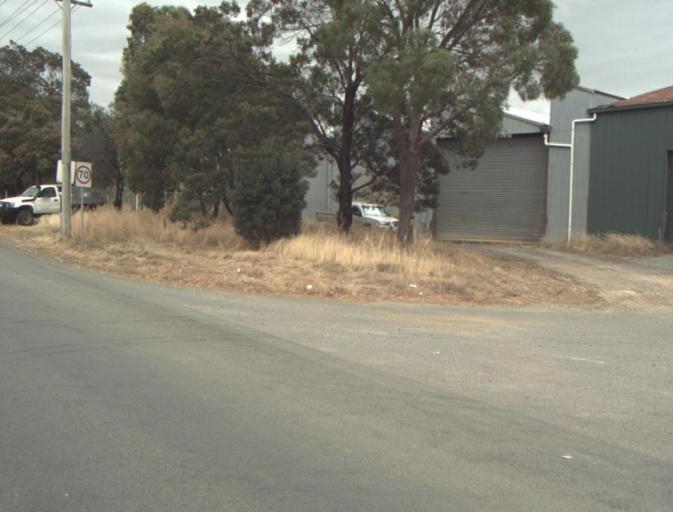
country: AU
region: Tasmania
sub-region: Launceston
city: Newstead
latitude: -41.4390
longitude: 147.1783
